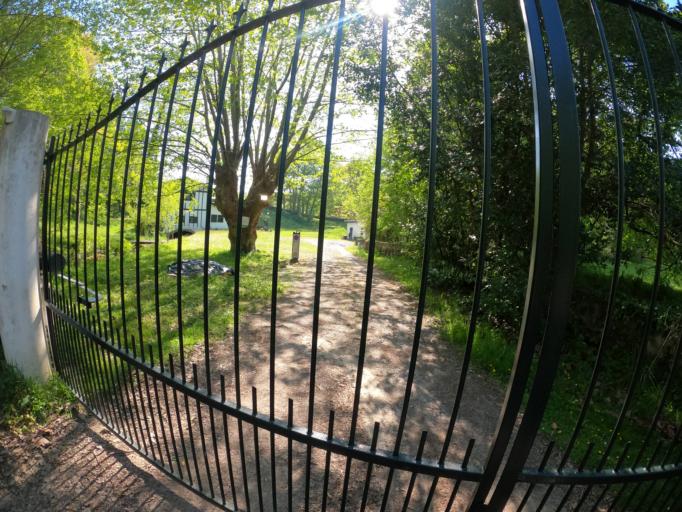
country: FR
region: Aquitaine
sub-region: Departement des Pyrenees-Atlantiques
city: Bassussarry
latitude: 43.4356
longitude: -1.4989
